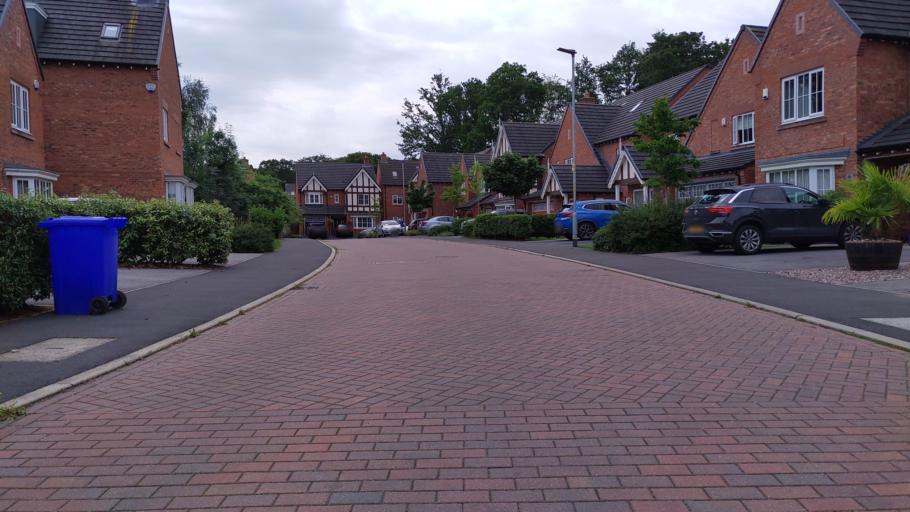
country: GB
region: England
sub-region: Lancashire
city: Chorley
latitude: 53.6381
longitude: -2.6259
